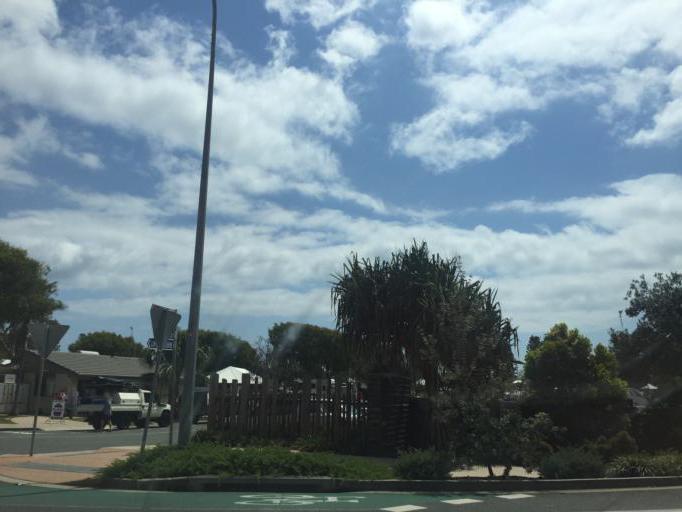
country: AU
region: Queensland
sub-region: Sunshine Coast
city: Coolum Beach
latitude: -26.5291
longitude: 153.0909
